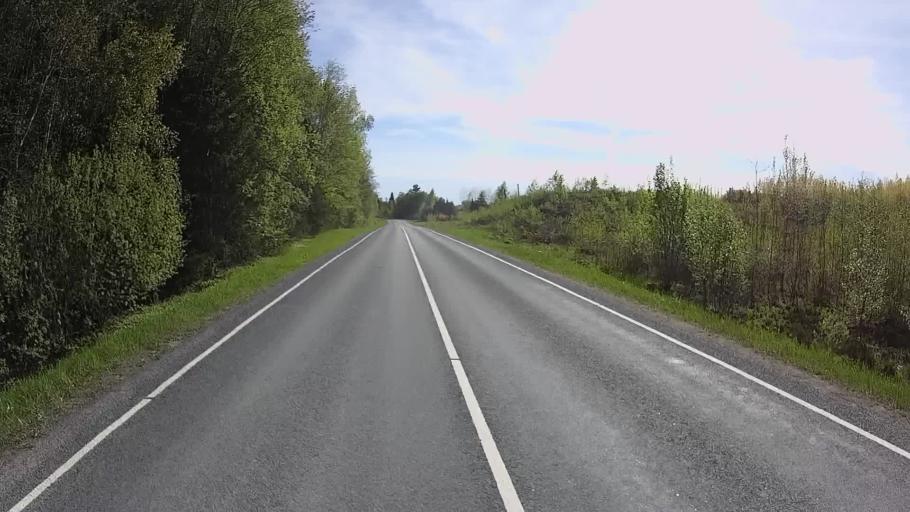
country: EE
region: Vorumaa
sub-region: Antsla vald
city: Vana-Antsla
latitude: 57.9636
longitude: 26.4560
